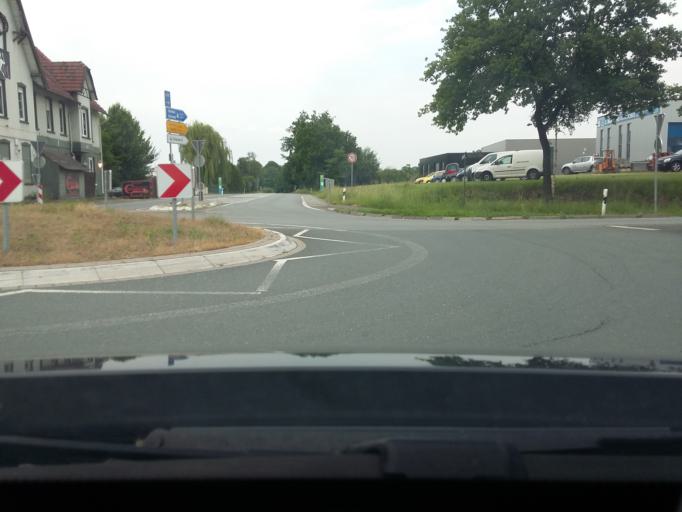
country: DE
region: North Rhine-Westphalia
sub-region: Regierungsbezirk Detmold
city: Vlotho
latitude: 52.1321
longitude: 8.8298
